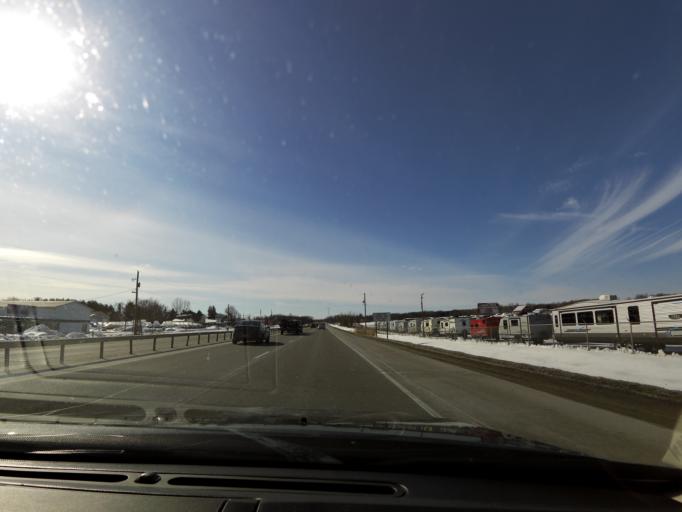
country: CA
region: Ontario
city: Orillia
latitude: 44.5034
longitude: -79.4845
